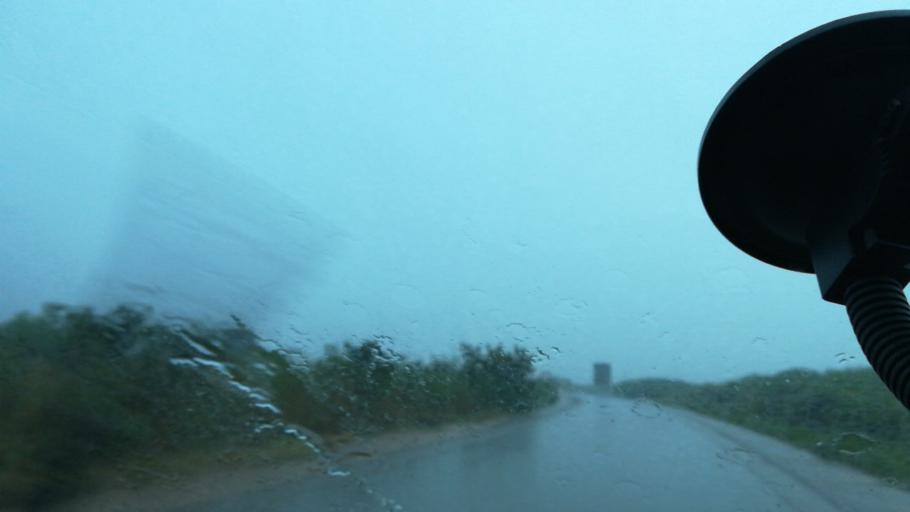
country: CD
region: Katanga
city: Lubumbashi
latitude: -11.5970
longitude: 27.4976
